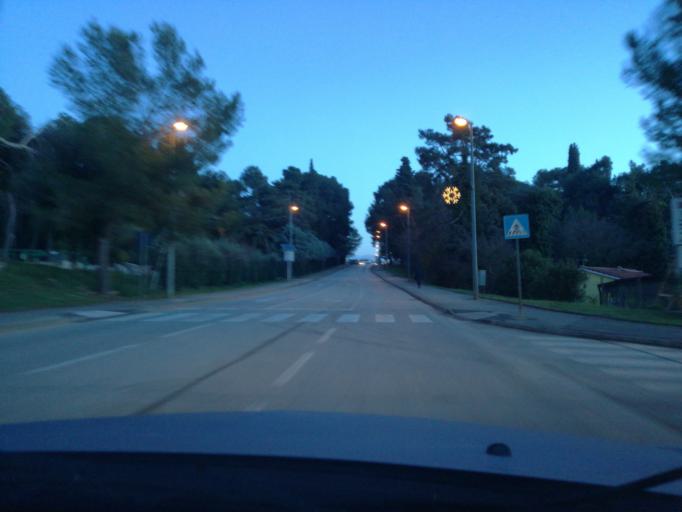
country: HR
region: Istarska
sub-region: Grad Rovinj
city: Rovinj
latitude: 45.0941
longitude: 13.6425
